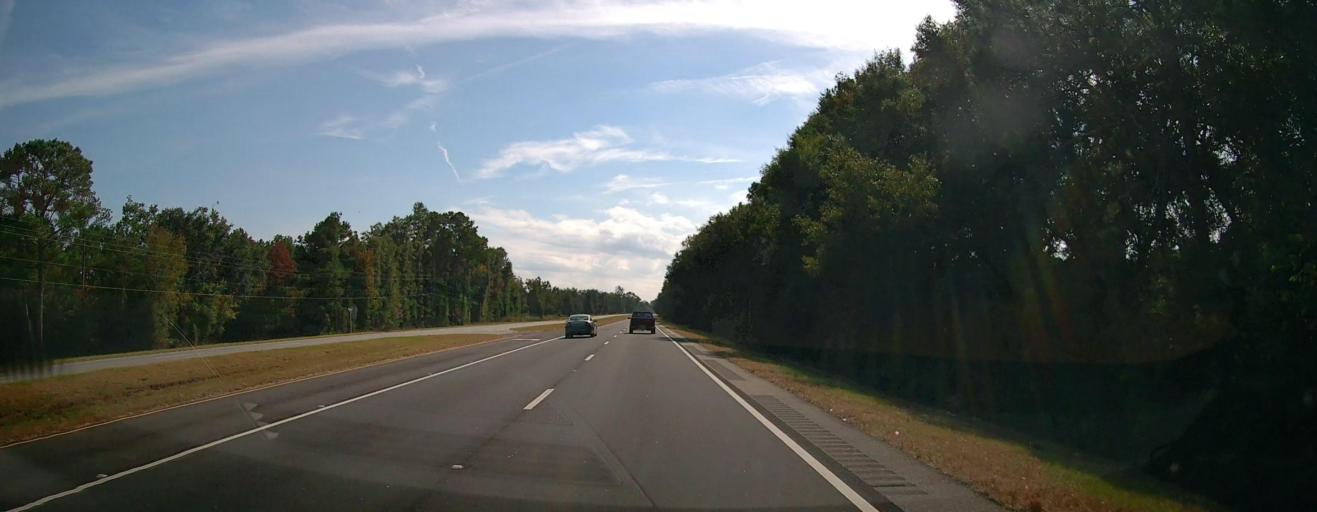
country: US
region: Georgia
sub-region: Dougherty County
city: Putney
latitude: 31.3954
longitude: -84.1465
